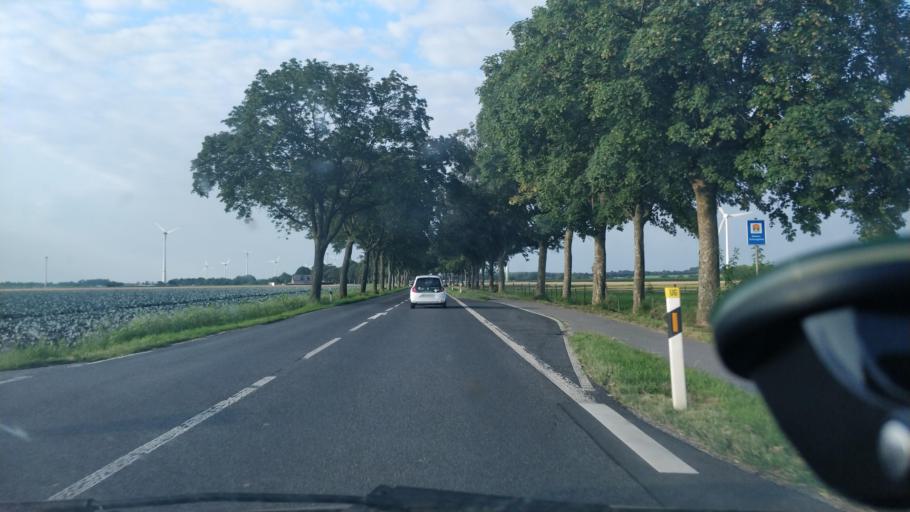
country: DE
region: North Rhine-Westphalia
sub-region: Regierungsbezirk Dusseldorf
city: Rheurdt
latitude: 51.4537
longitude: 6.4293
